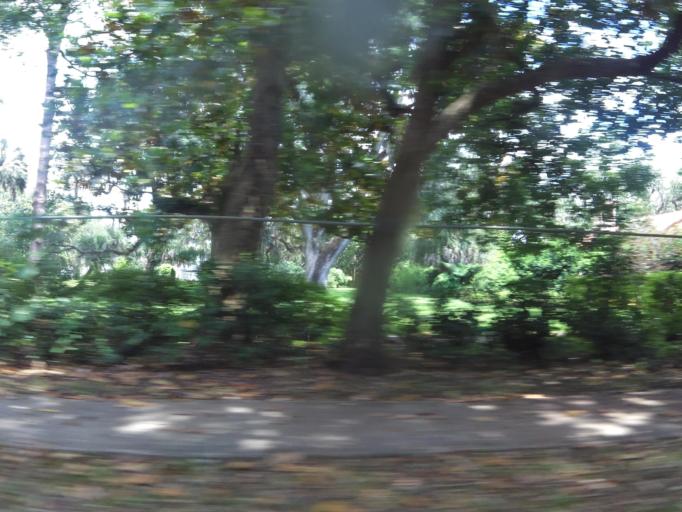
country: US
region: Florida
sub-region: Clay County
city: Orange Park
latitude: 30.1653
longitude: -81.6974
